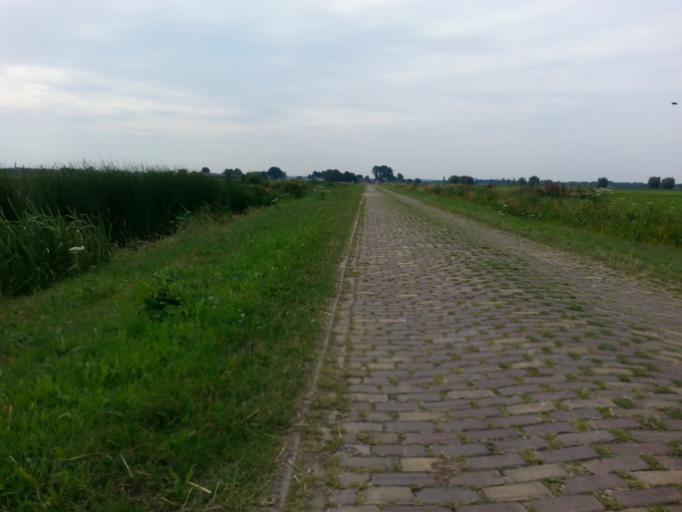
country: NL
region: Utrecht
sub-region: Gemeente Soest
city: Soest
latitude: 52.1937
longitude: 5.3234
